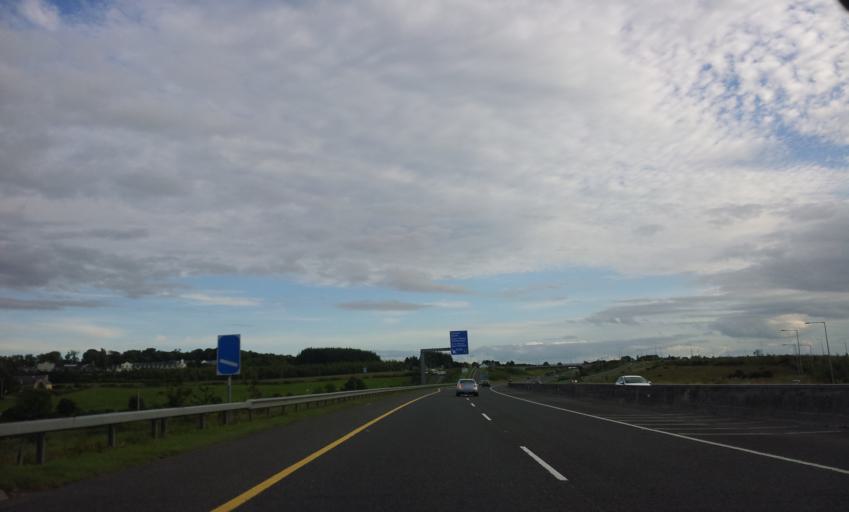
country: IE
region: Munster
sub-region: An Clar
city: Newmarket on Fergus
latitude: 52.7949
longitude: -8.9210
